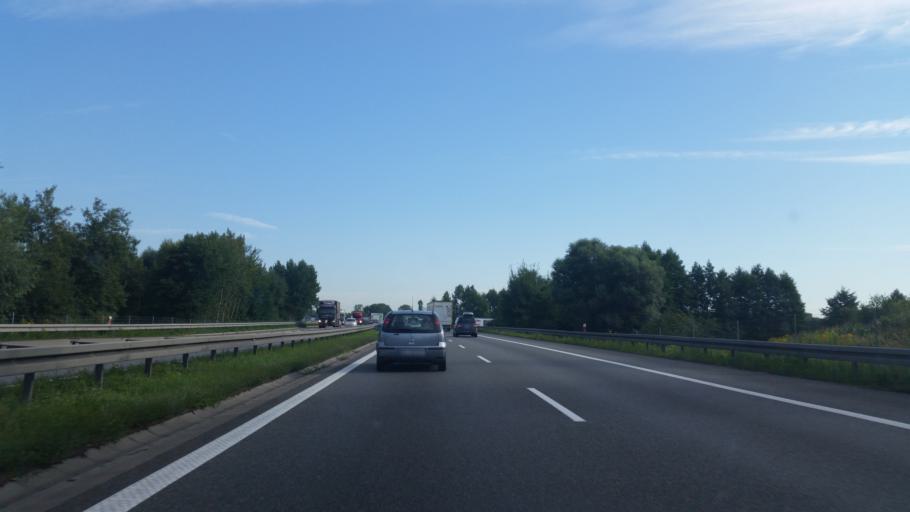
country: PL
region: Lesser Poland Voivodeship
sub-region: Powiat krakowski
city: Kryspinow
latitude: 50.0527
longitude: 19.8092
